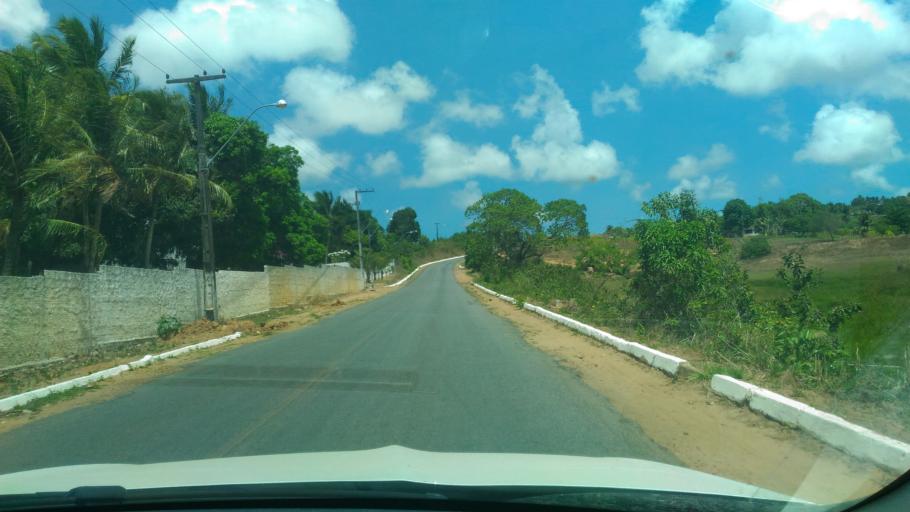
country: BR
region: Paraiba
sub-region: Conde
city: Conde
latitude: -7.2622
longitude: -34.9212
